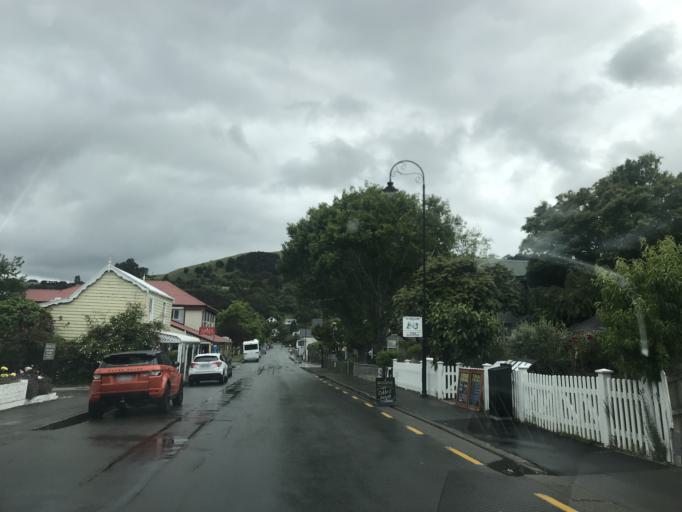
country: NZ
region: Canterbury
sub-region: Christchurch City
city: Christchurch
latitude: -43.8037
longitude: 172.9682
